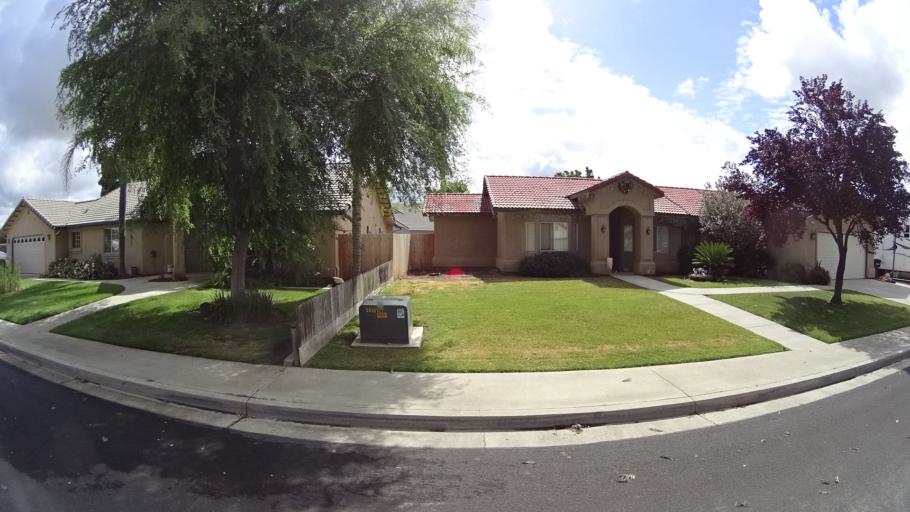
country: US
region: California
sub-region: Kings County
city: Lucerne
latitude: 36.3679
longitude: -119.6495
